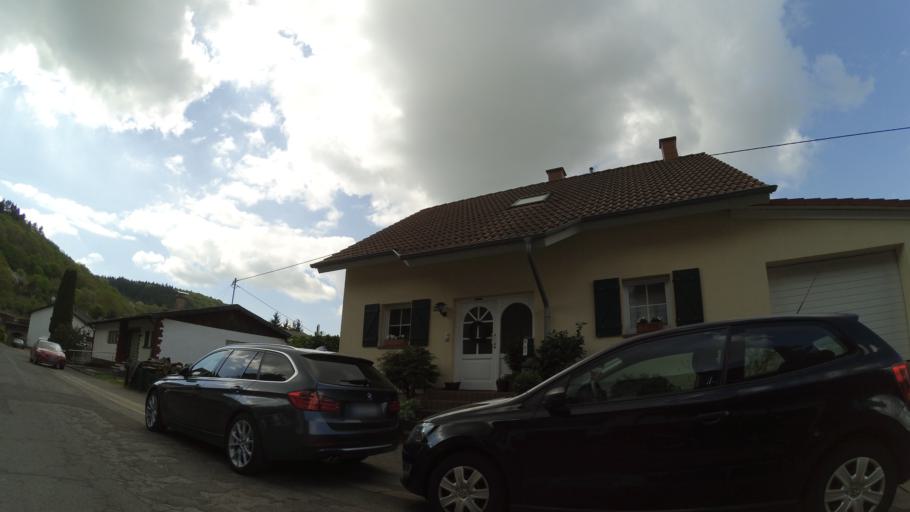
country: DE
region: Saarland
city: Wadern
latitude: 49.4994
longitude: 6.8715
